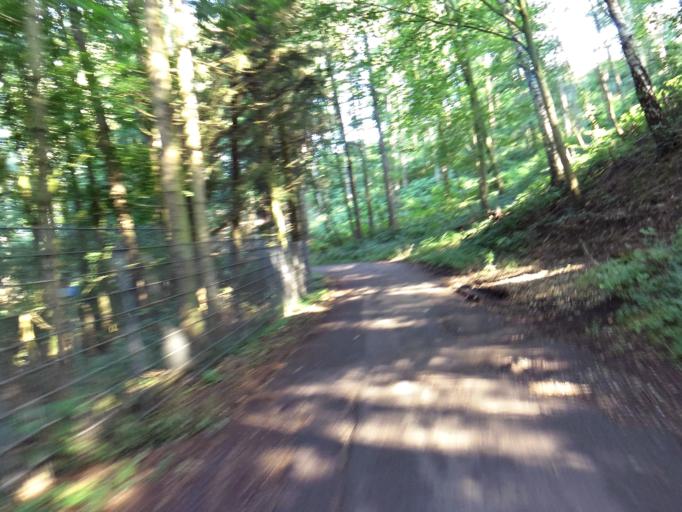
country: DE
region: North Rhine-Westphalia
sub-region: Regierungsbezirk Koln
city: Alsdorf
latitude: 50.8659
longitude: 6.1349
